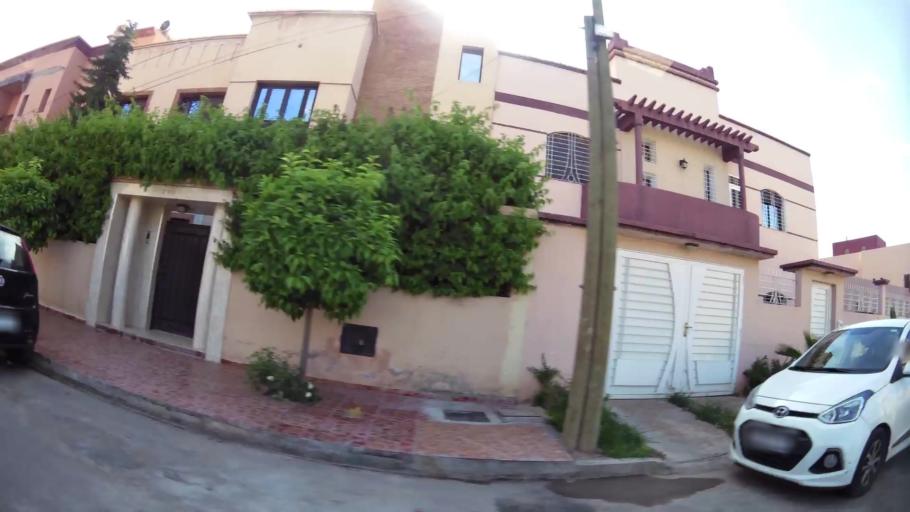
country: MA
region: Marrakech-Tensift-Al Haouz
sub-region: Marrakech
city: Marrakesh
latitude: 31.6463
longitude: -8.0433
